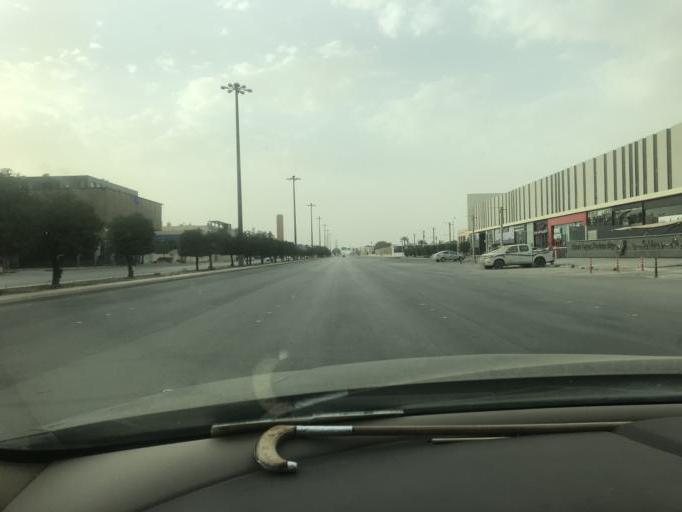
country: SA
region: Ar Riyad
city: Riyadh
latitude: 24.7885
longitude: 46.6592
